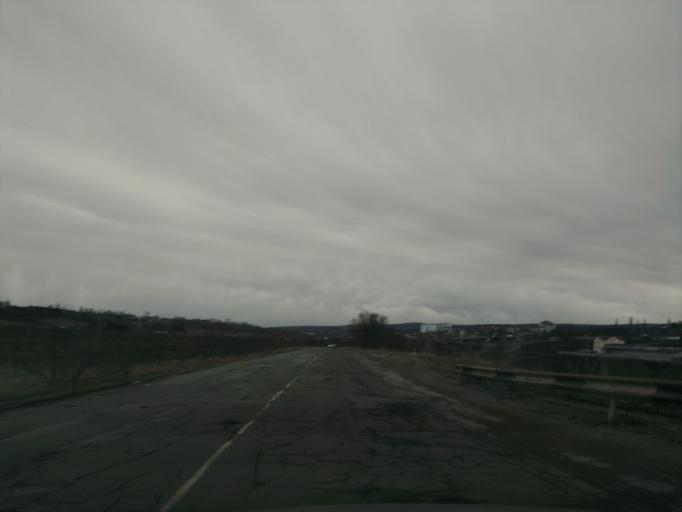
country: MD
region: Laloveni
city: Ialoveni
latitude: 46.9720
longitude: 28.7526
